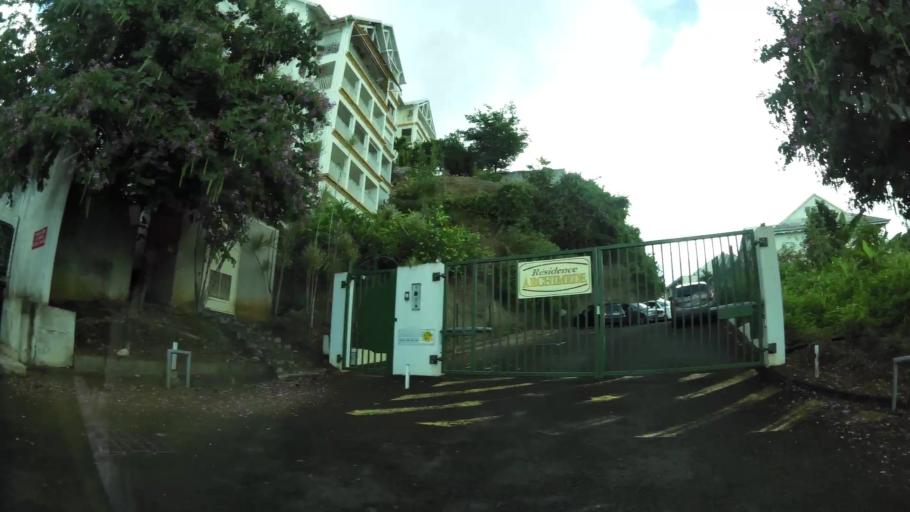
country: GP
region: Guadeloupe
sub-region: Guadeloupe
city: Pointe-a-Pitre
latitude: 16.2490
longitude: -61.5171
